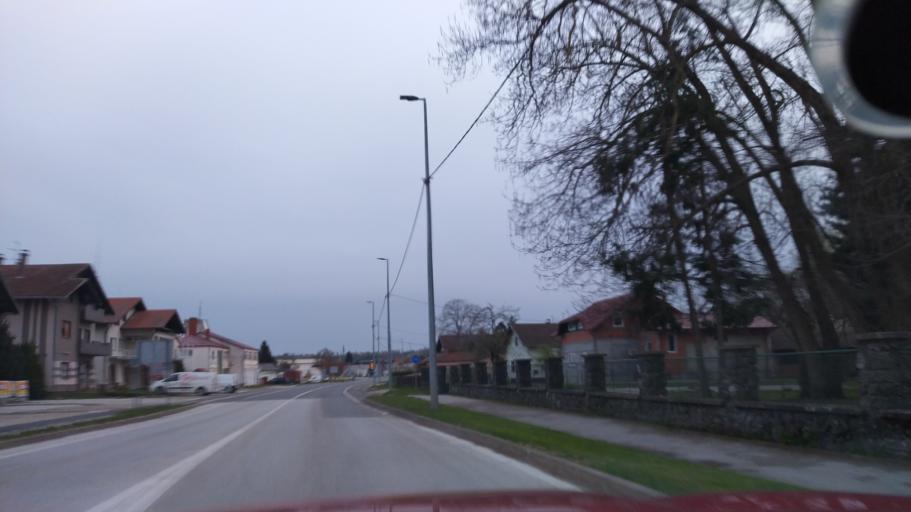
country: HR
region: Varazdinska
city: Ludbreg
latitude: 46.2465
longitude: 16.6214
